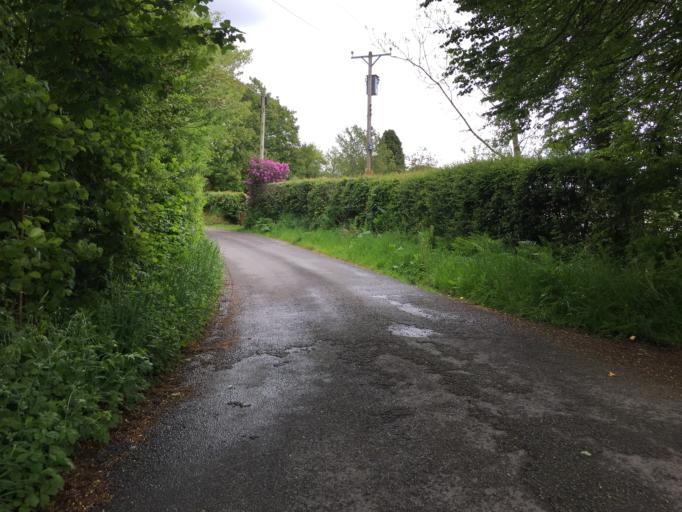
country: GB
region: Wales
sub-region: County of Ceredigion
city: Llangybi
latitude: 52.1700
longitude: -4.0520
